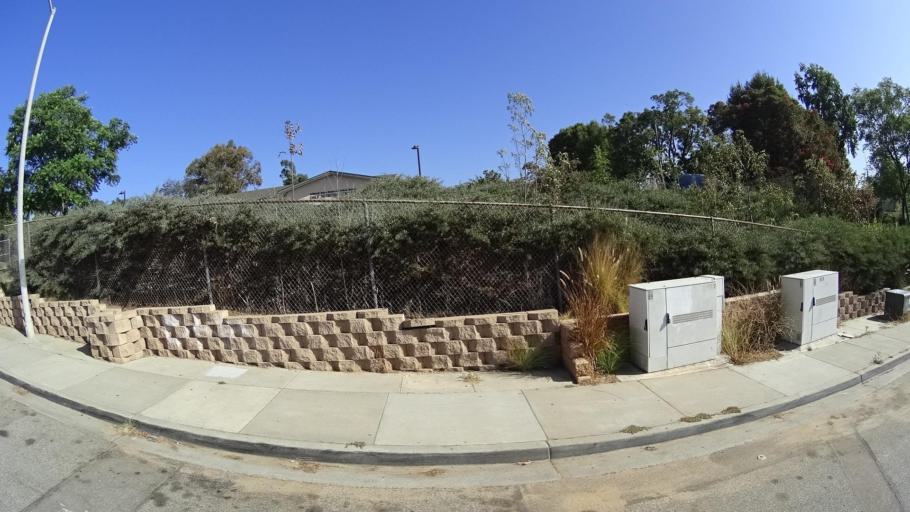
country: US
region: California
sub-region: San Diego County
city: Fallbrook
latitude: 33.3767
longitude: -117.2563
